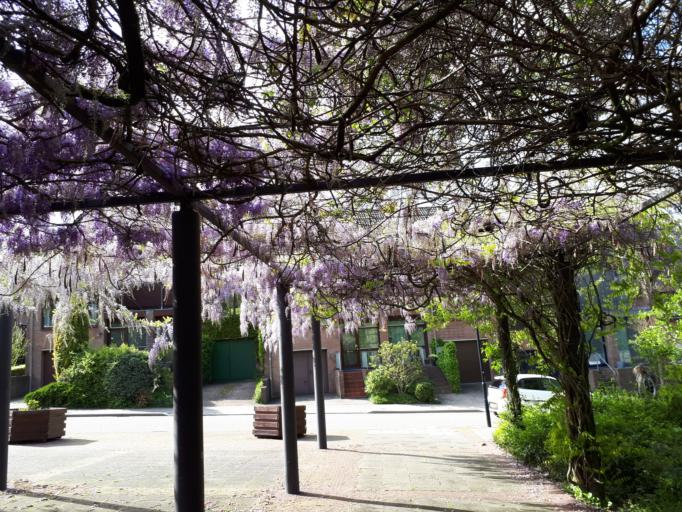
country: NL
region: Limburg
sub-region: Gemeente Vaals
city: Vaals
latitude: 50.7725
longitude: 6.0113
